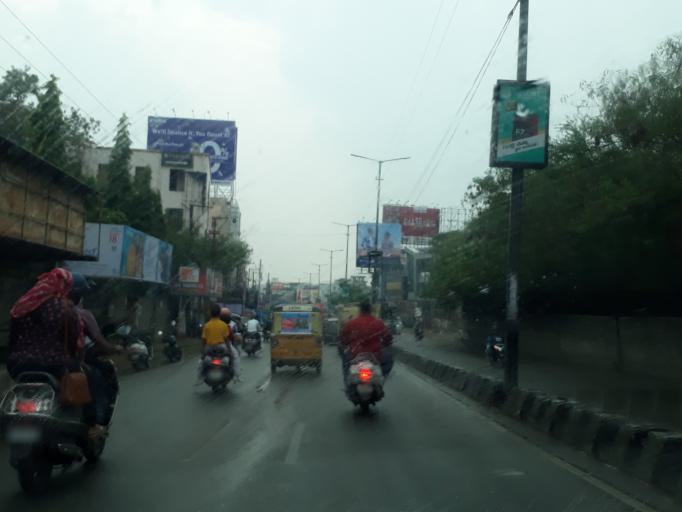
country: IN
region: Telangana
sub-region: Hyderabad
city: Malkajgiri
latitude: 17.4653
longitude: 78.5044
